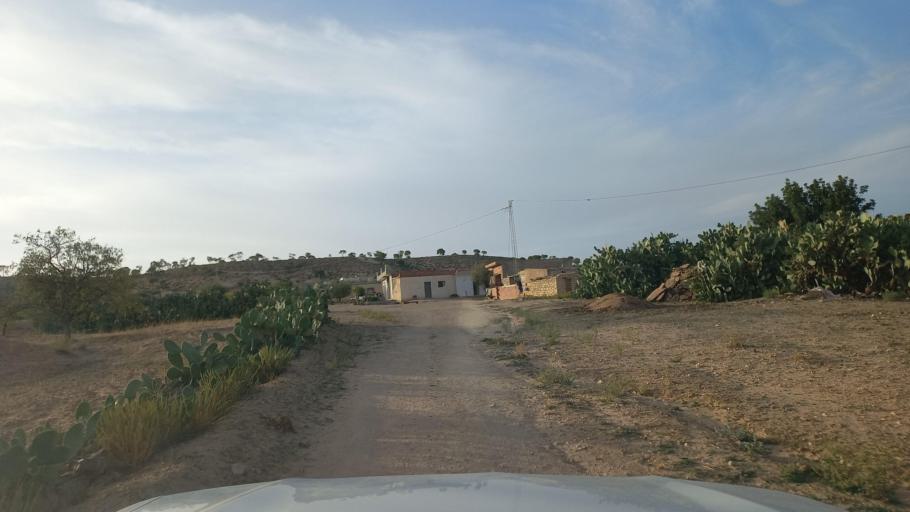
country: TN
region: Al Qasrayn
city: Sbiba
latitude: 35.4050
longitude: 8.8985
